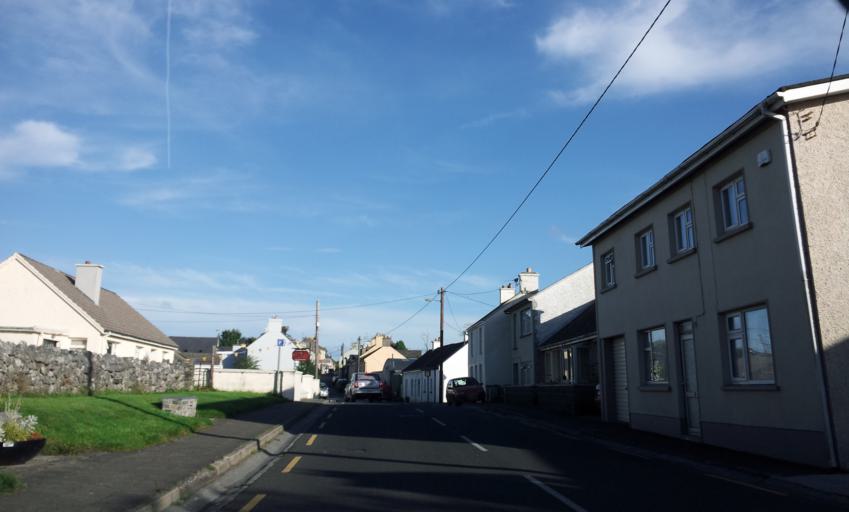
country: IE
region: Munster
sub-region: An Clar
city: Ennis
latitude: 52.9464
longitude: -9.0679
